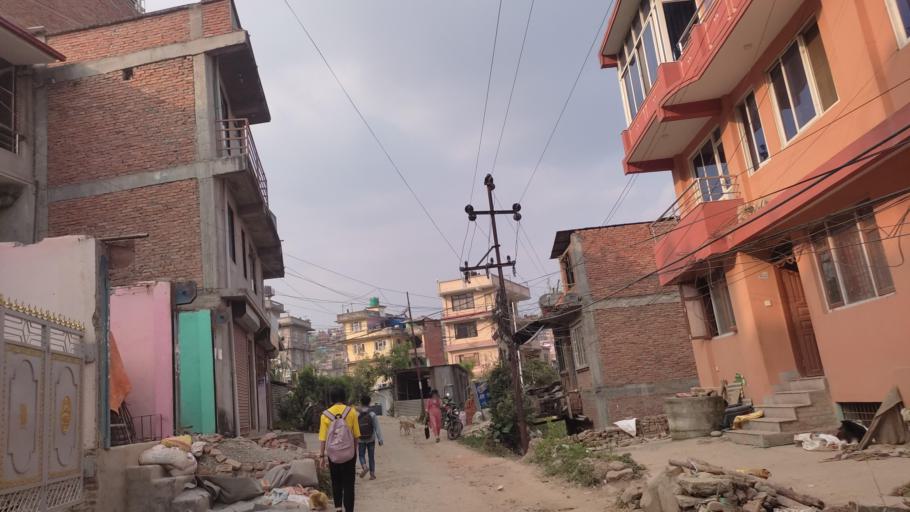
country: NP
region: Central Region
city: Kirtipur
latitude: 27.6722
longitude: 85.2770
